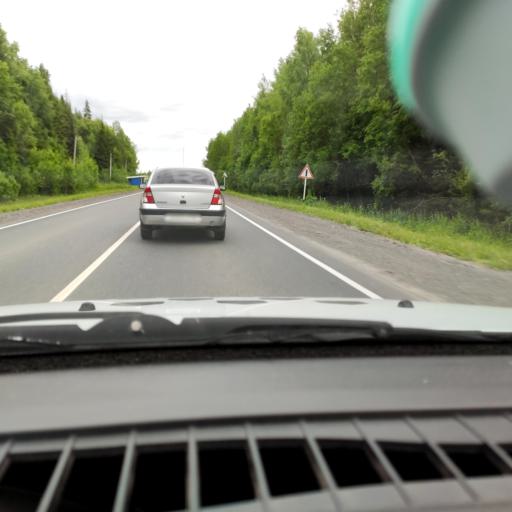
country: RU
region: Perm
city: Chusovoy
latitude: 58.2325
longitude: 57.8269
